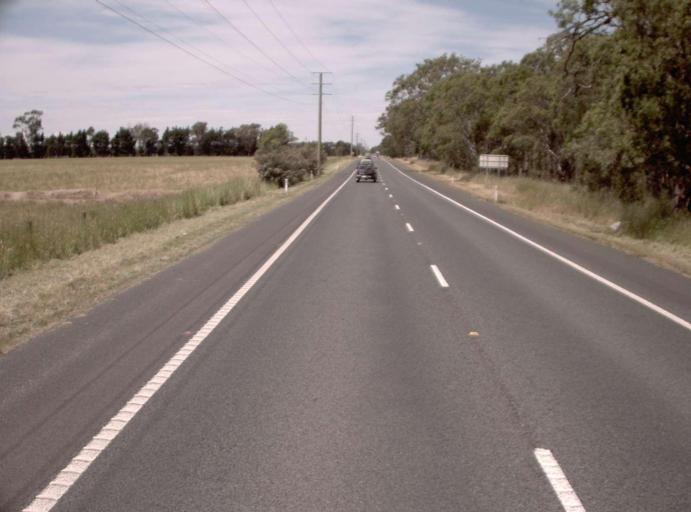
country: AU
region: Victoria
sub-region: Latrobe
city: Traralgon
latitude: -38.1746
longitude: 146.6546
